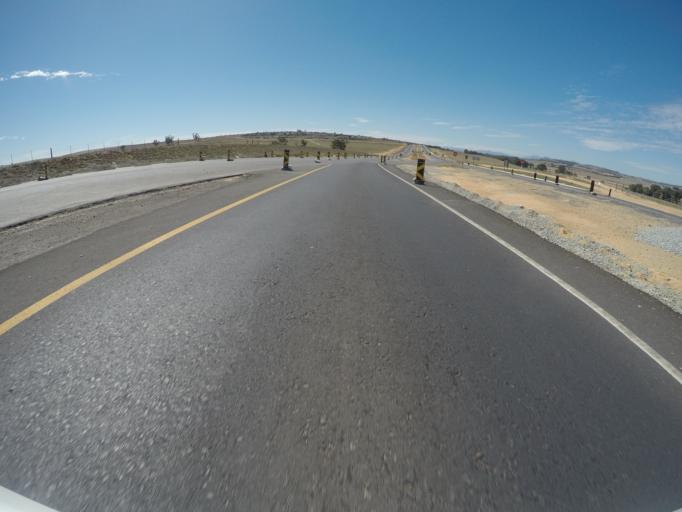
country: ZA
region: Western Cape
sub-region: West Coast District Municipality
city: Malmesbury
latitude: -33.4785
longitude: 18.6842
